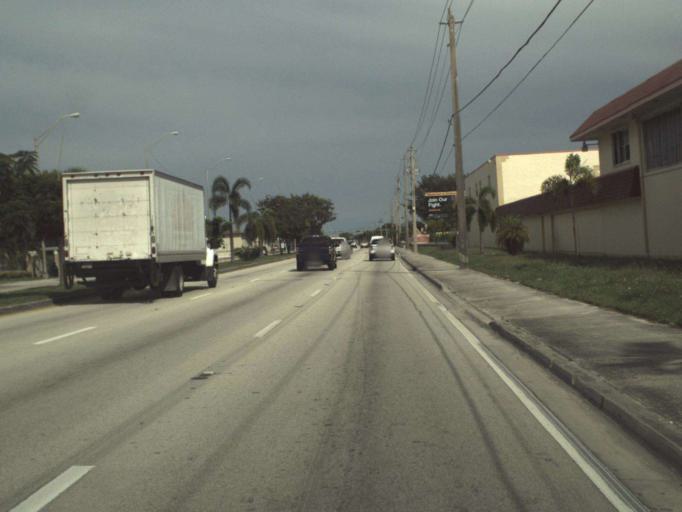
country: US
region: Florida
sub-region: Miami-Dade County
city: Westview
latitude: 25.8826
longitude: -80.2384
